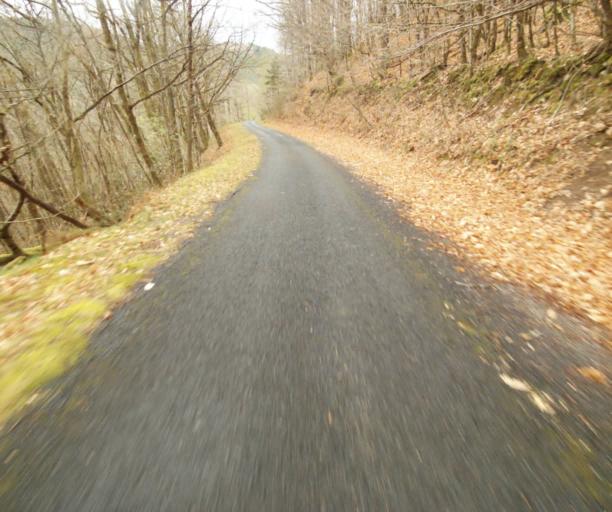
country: FR
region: Limousin
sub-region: Departement de la Correze
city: Saint-Privat
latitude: 45.2125
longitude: 2.0354
